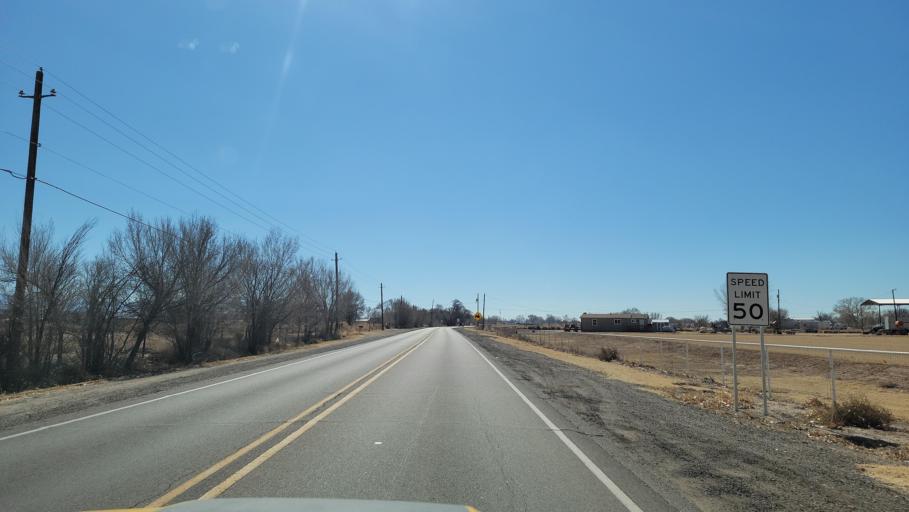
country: US
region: New Mexico
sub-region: Bernalillo County
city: South Valley
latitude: 34.9459
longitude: -106.6930
